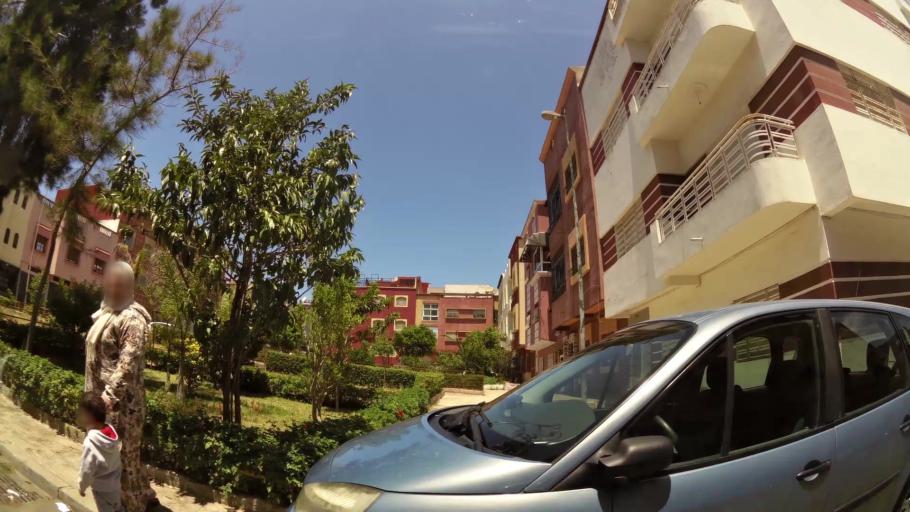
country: MA
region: Gharb-Chrarda-Beni Hssen
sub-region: Kenitra Province
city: Kenitra
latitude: 34.2538
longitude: -6.6176
